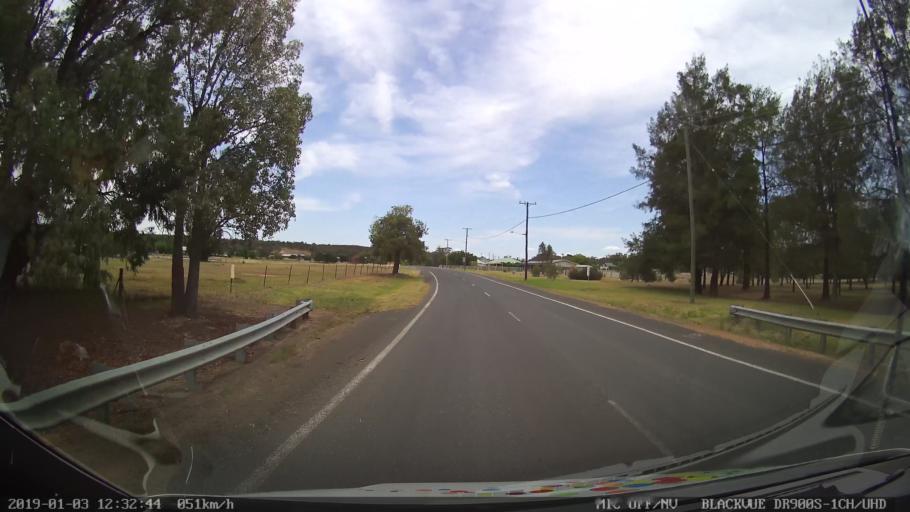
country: AU
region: New South Wales
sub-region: Weddin
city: Grenfell
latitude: -33.8912
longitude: 148.1619
